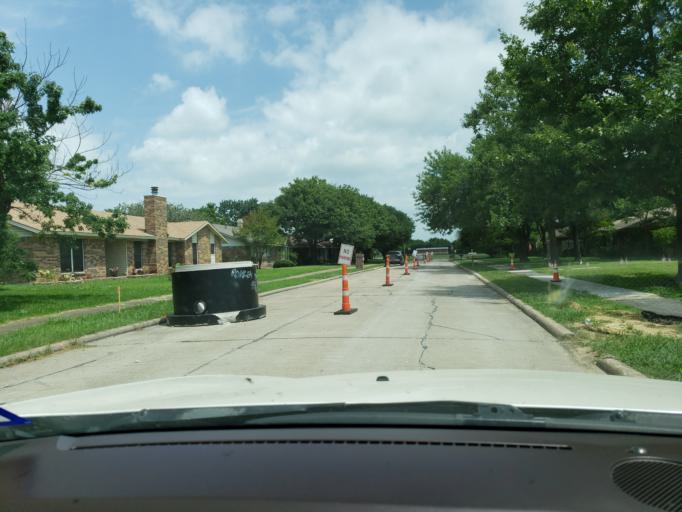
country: US
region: Texas
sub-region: Dallas County
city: Rowlett
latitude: 32.8987
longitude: -96.5610
